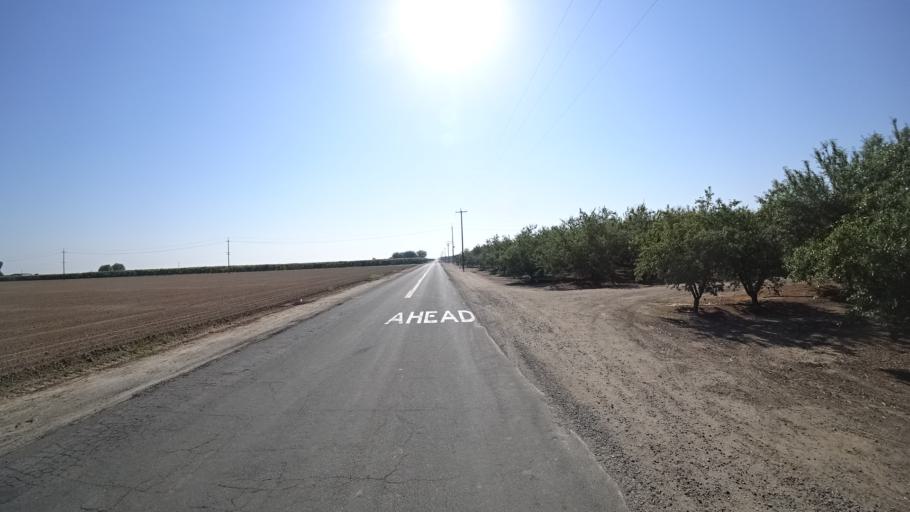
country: US
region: California
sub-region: Kings County
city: Lucerne
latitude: 36.3865
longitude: -119.5851
